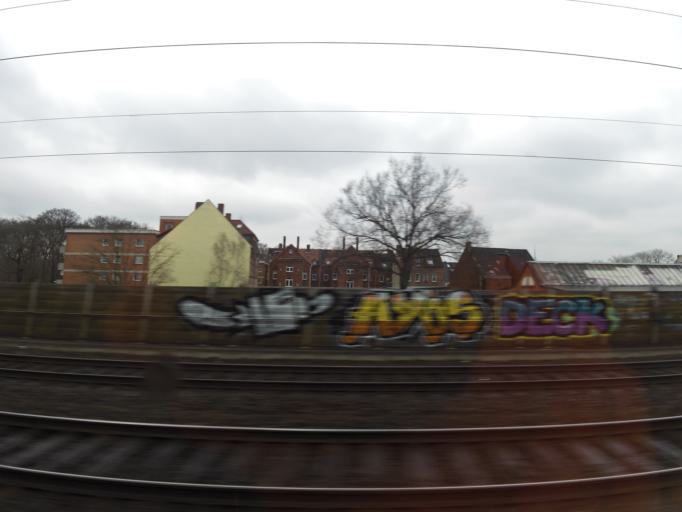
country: DE
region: Lower Saxony
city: Hannover
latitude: 52.3730
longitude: 9.7834
